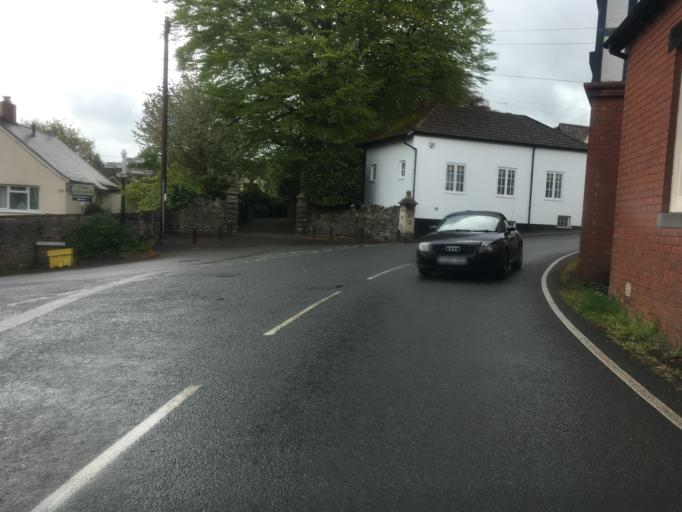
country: GB
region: England
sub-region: North Somerset
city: Blagdon
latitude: 51.3288
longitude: -2.7182
